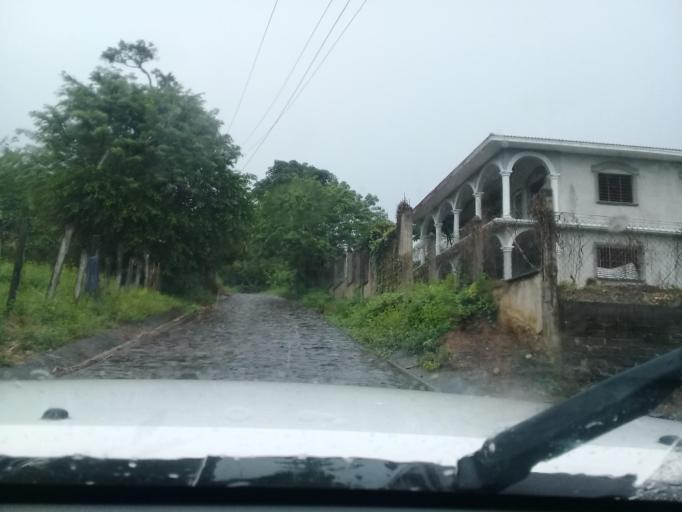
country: MX
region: Veracruz
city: Santiago Tuxtla
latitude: 18.4602
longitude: -95.3131
